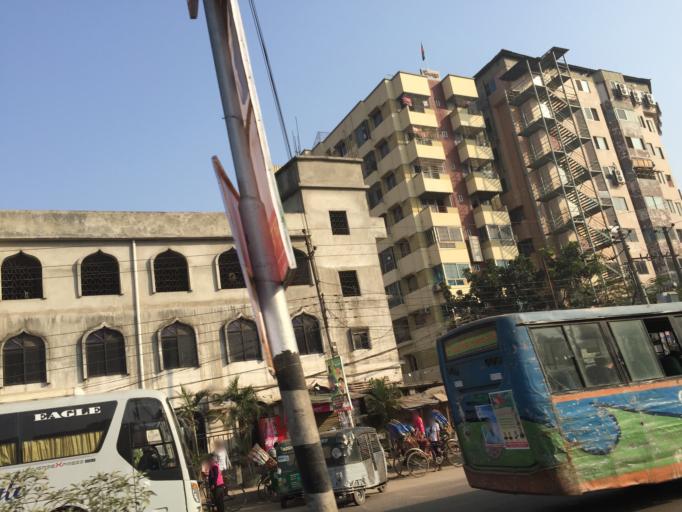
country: BD
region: Dhaka
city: Azimpur
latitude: 23.7787
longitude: 90.3595
